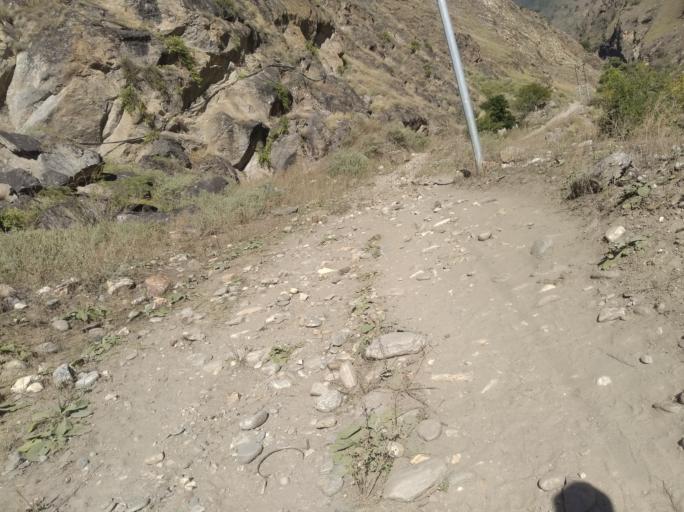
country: NP
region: Mid Western
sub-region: Karnali Zone
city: Jumla
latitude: 28.9368
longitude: 82.9278
